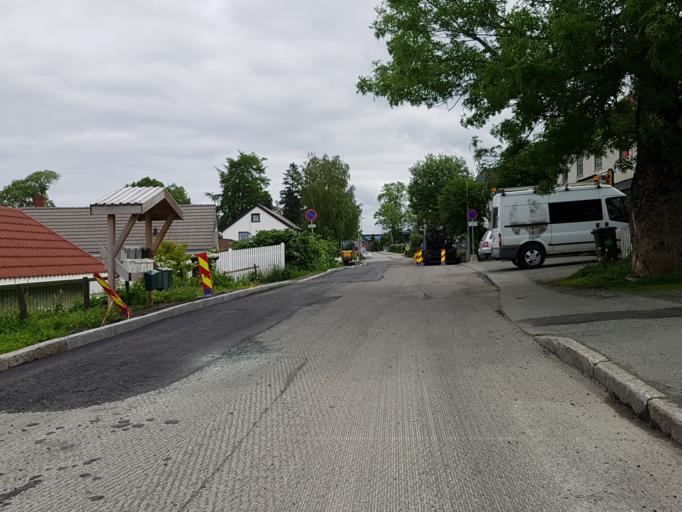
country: NO
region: Sor-Trondelag
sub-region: Trondheim
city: Trondheim
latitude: 63.4363
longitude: 10.4464
